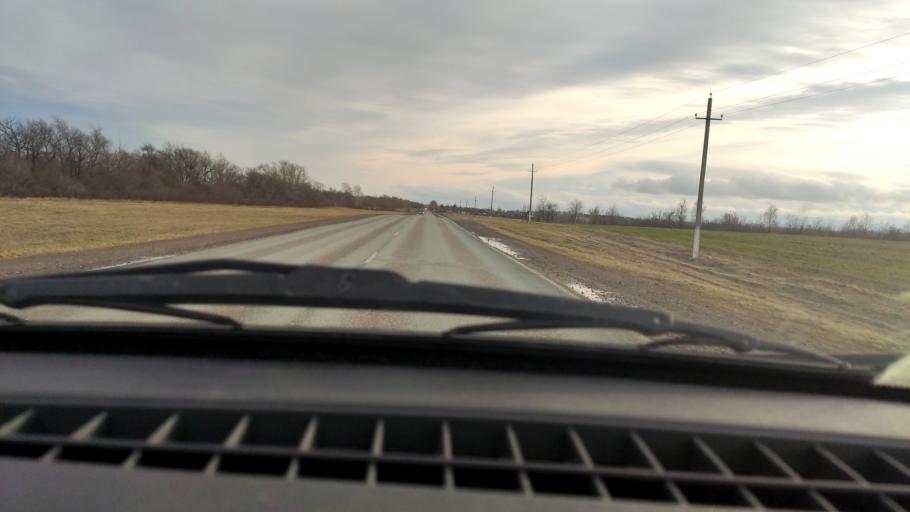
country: RU
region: Bashkortostan
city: Davlekanovo
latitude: 54.3066
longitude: 55.1389
